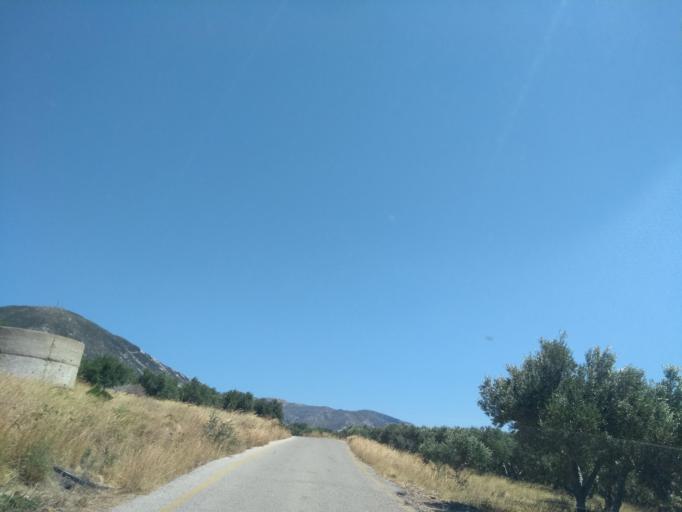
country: GR
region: Crete
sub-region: Nomos Chanias
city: Vryses
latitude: 35.3590
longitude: 23.5423
